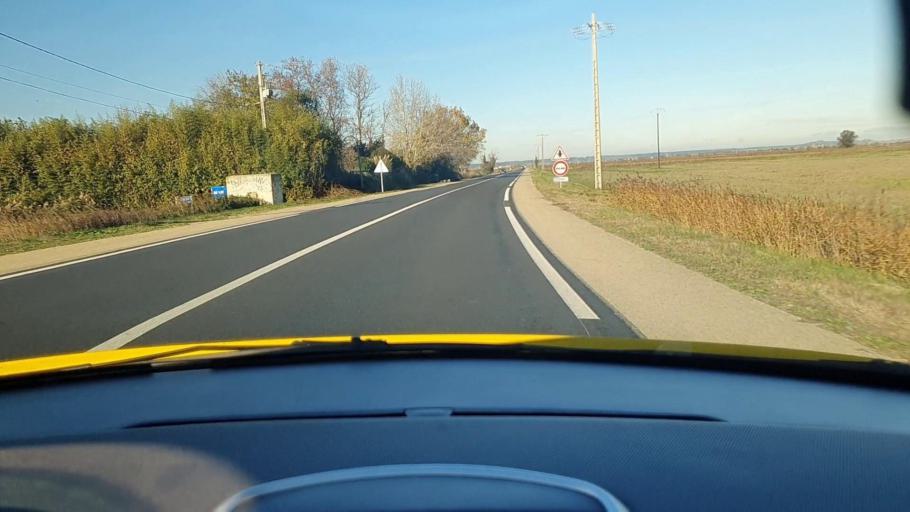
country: FR
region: Languedoc-Roussillon
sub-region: Departement du Gard
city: Bellegarde
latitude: 43.7108
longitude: 4.5491
